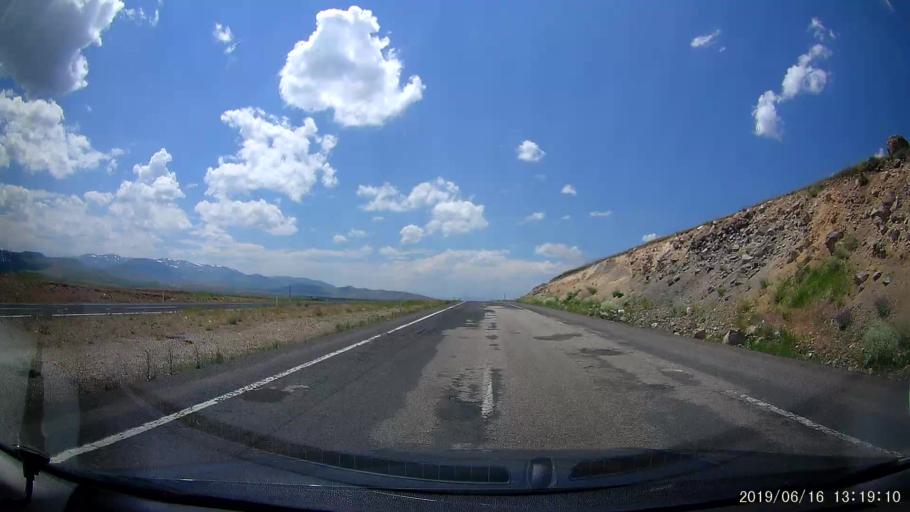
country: TR
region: Agri
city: Taslicay
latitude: 39.6327
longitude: 43.4139
